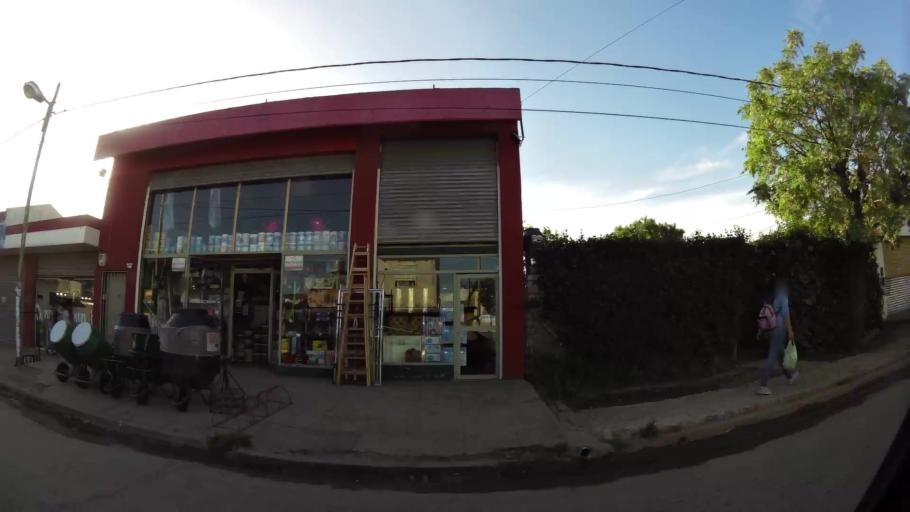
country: AR
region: Buenos Aires
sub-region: Partido de Quilmes
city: Quilmes
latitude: -34.8177
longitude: -58.2062
